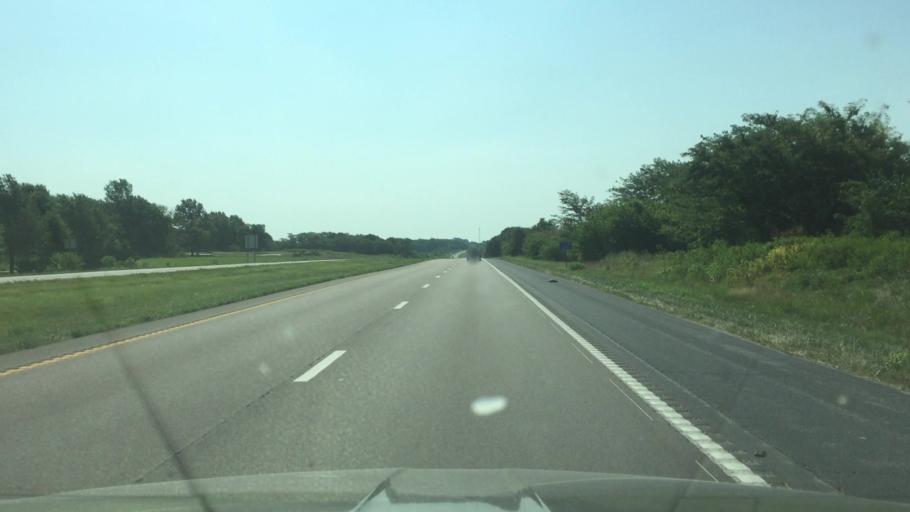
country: US
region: Missouri
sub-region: Pettis County
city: La Monte
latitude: 38.7467
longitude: -93.3387
